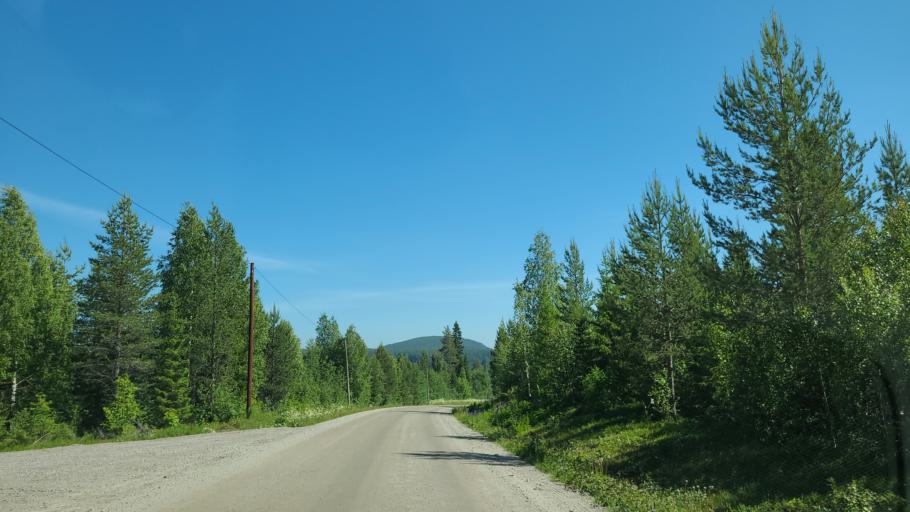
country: SE
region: Vaesterbotten
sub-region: Bjurholms Kommun
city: Bjurholm
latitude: 63.7020
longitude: 18.9234
